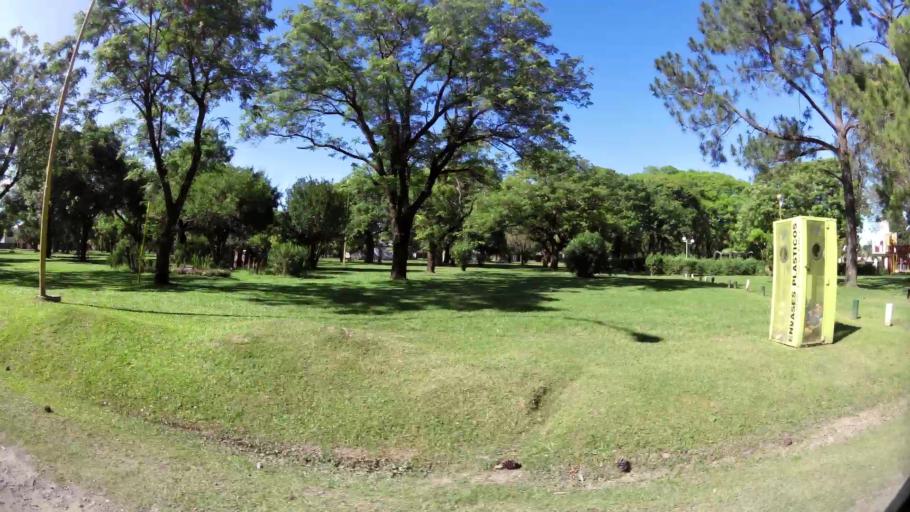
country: AR
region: Santa Fe
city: Esperanza
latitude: -31.4488
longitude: -60.9179
